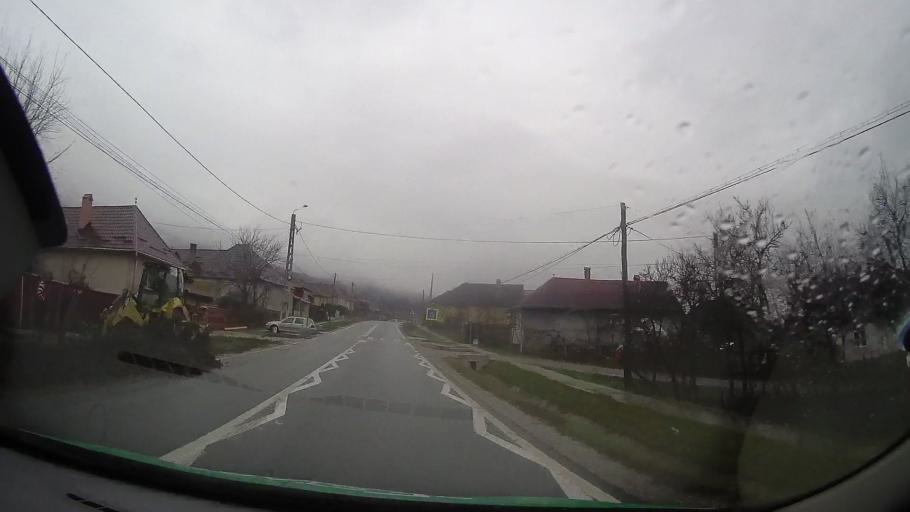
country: RO
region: Bistrita-Nasaud
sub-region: Comuna Galatii Bistritei
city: Galatii Bistritei
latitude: 46.9946
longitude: 24.4178
